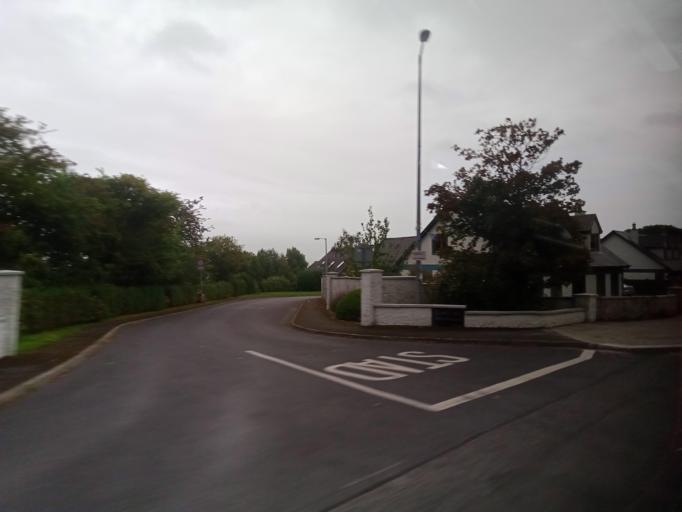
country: IE
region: Munster
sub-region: Waterford
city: Dungarvan
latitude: 52.0480
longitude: -7.5969
